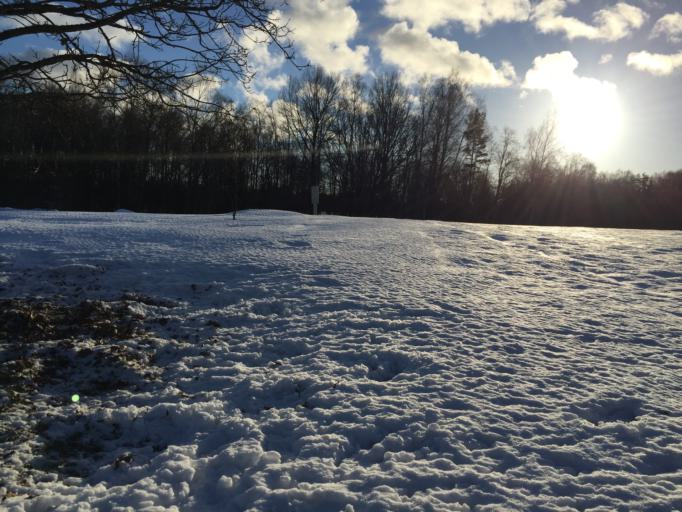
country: LV
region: Lielvarde
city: Lielvarde
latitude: 56.6772
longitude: 24.8775
